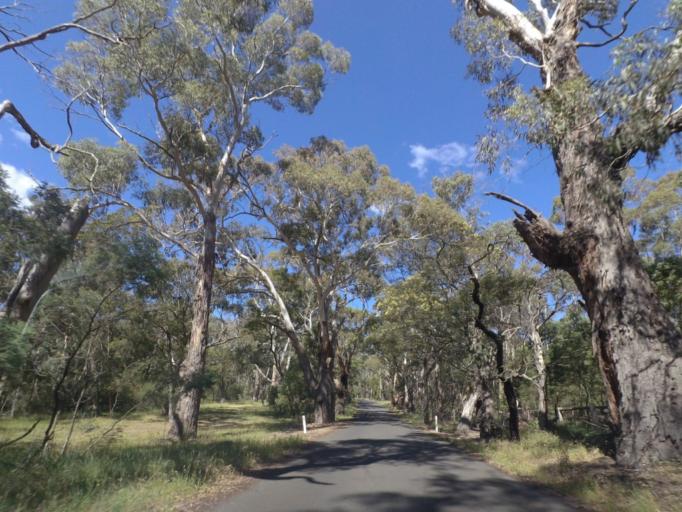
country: AU
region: Victoria
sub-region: Hume
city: Sunbury
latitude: -37.4212
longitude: 144.6212
